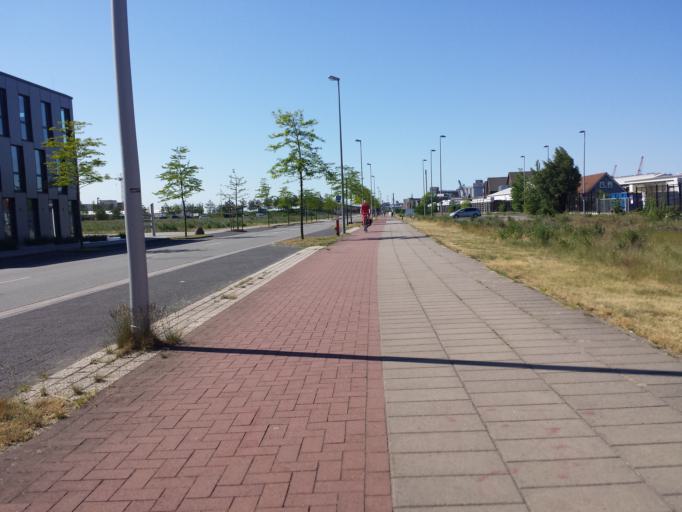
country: DE
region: Bremen
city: Bremen
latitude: 53.0994
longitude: 8.7662
